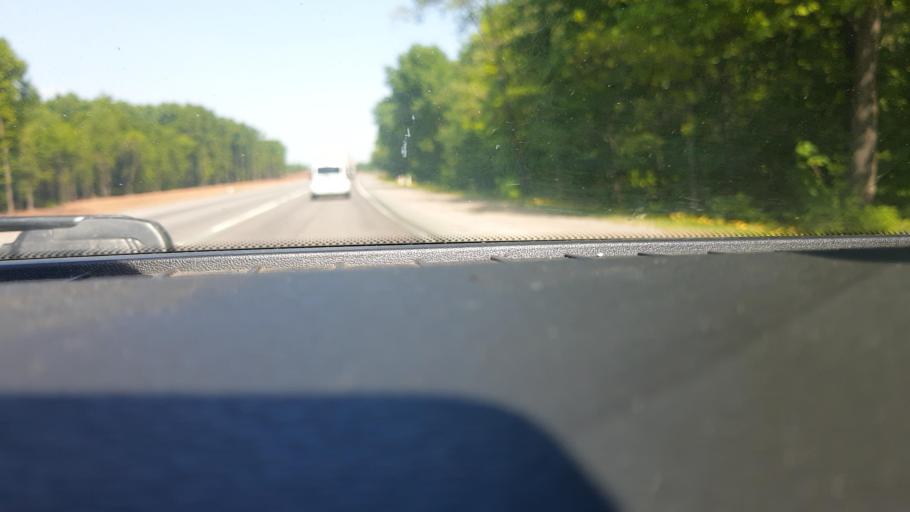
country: RU
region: Bashkortostan
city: Iglino
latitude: 54.7236
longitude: 56.2434
